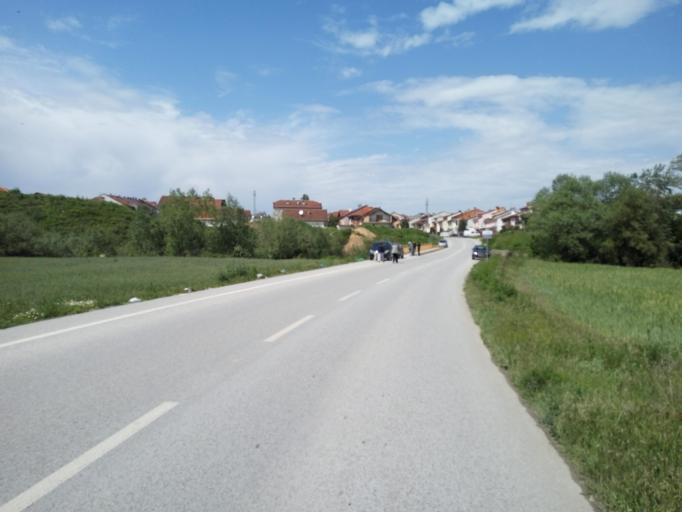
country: XK
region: Gjakova
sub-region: Komuna e Gjakoves
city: Gjakove
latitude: 42.3649
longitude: 20.4355
